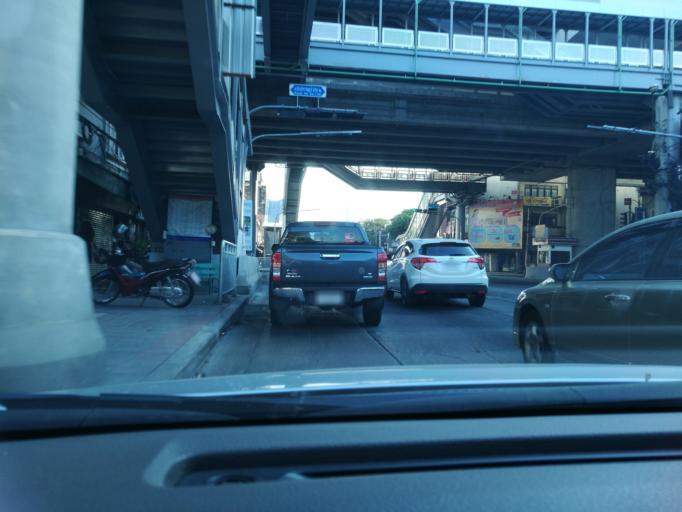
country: TH
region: Bangkok
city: Bang Sue
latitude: 13.8068
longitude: 100.5216
